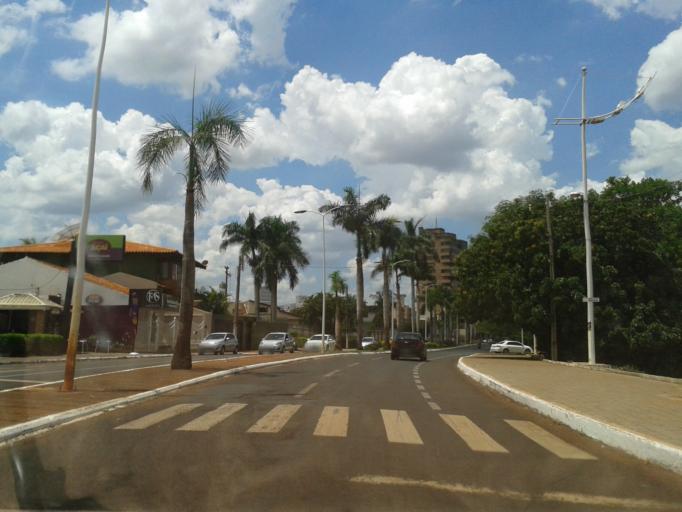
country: BR
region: Goias
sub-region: Itumbiara
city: Itumbiara
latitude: -18.4153
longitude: -49.2128
